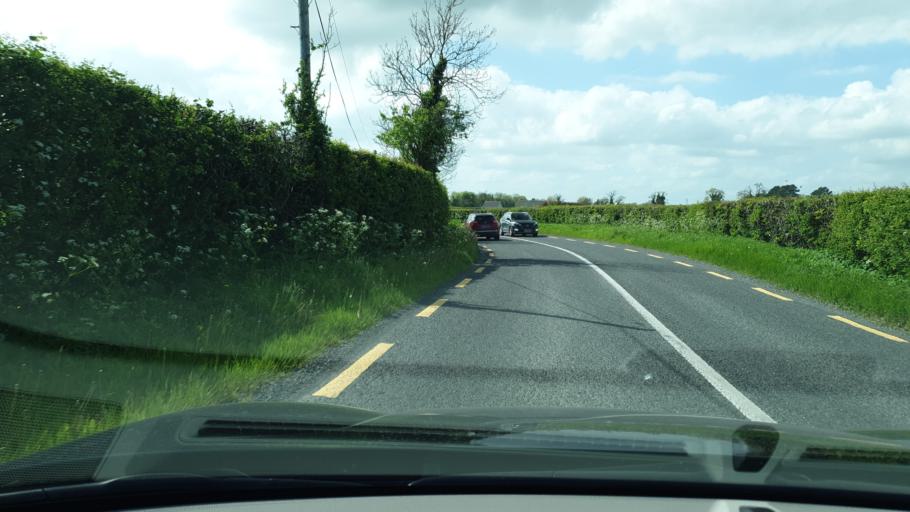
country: IE
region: Leinster
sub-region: An Mhi
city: Dunshaughlin
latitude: 53.5213
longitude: -6.5207
